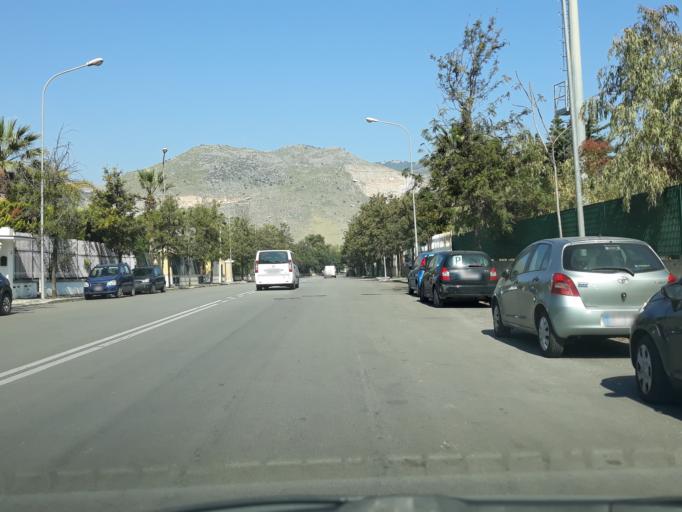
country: IT
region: Sicily
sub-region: Palermo
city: Palermo
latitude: 38.1222
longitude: 13.3047
